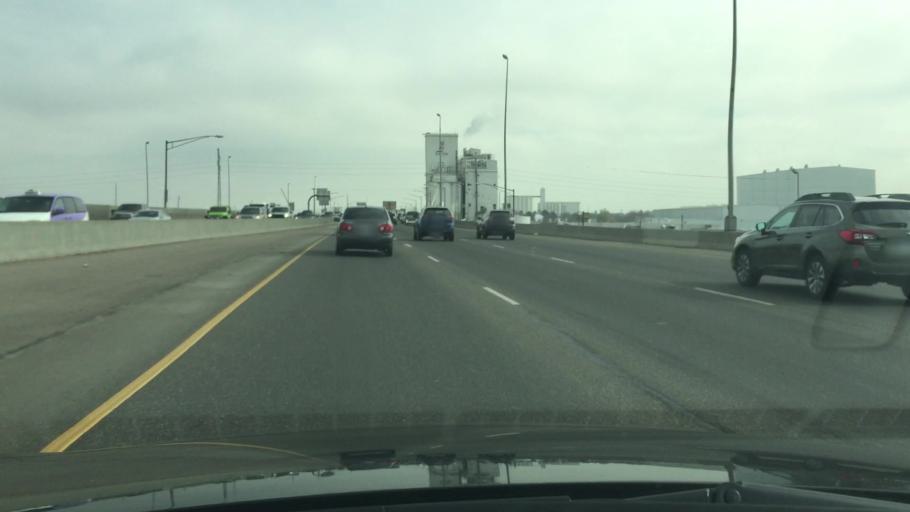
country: US
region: Colorado
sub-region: Adams County
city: Commerce City
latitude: 39.7799
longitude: -104.9665
